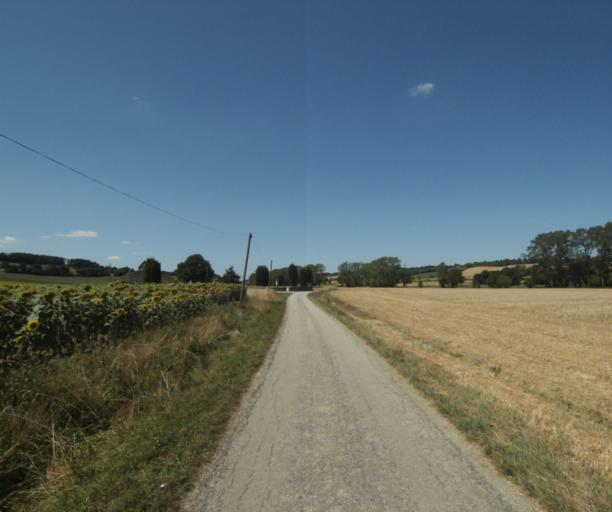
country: FR
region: Midi-Pyrenees
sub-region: Departement de la Haute-Garonne
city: Saint-Felix-Lauragais
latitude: 43.4865
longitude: 1.8741
